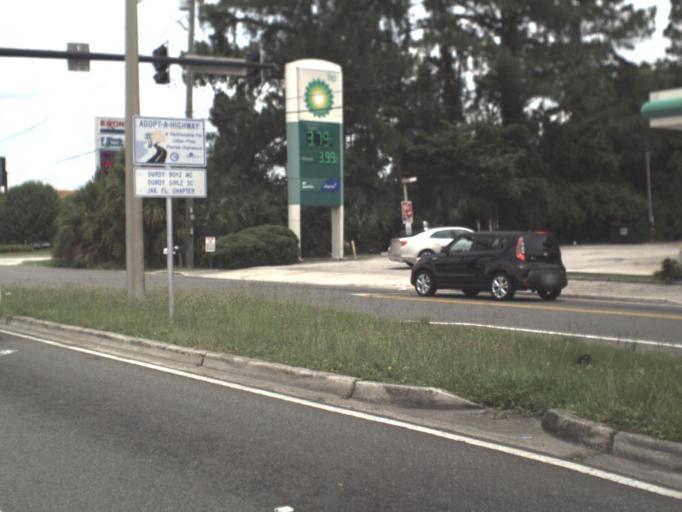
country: US
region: Florida
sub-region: Duval County
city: Jacksonville
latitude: 30.4821
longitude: -81.6468
